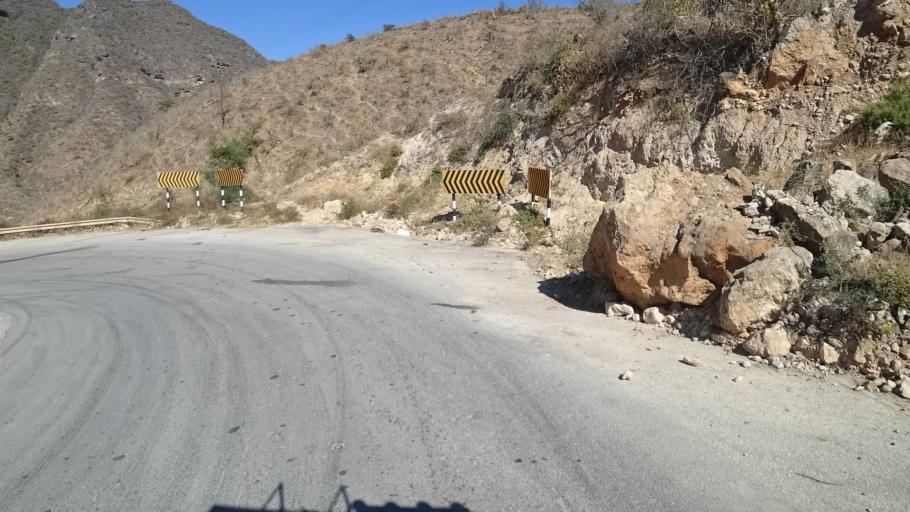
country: YE
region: Al Mahrah
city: Hawf
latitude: 16.7475
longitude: 53.4129
